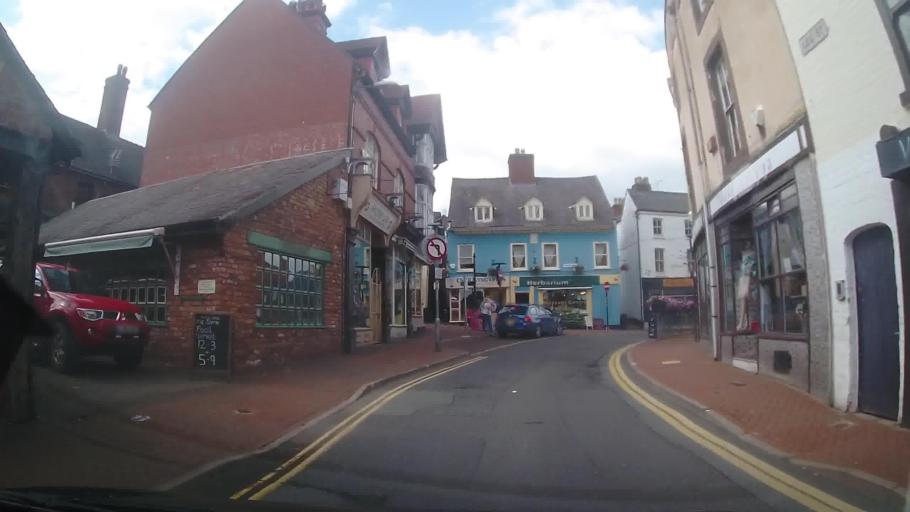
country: GB
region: England
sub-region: Shropshire
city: Oswestry
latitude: 52.8603
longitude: -3.0539
